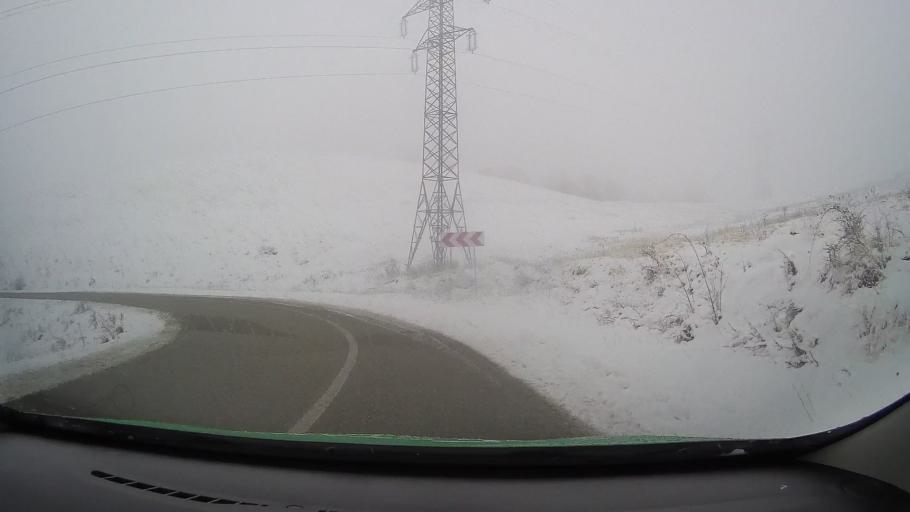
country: RO
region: Hunedoara
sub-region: Comuna Unirea
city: Unirea
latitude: 45.6615
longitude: 22.9098
